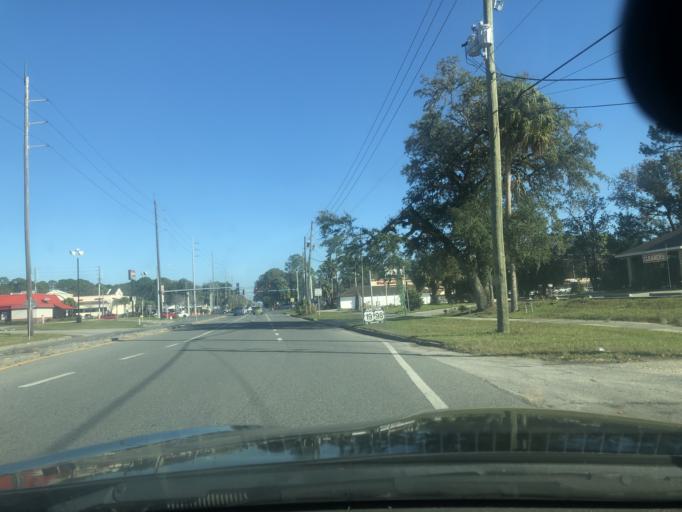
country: US
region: Florida
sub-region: Citrus County
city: Homosassa Springs
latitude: 28.8036
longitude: -82.5781
